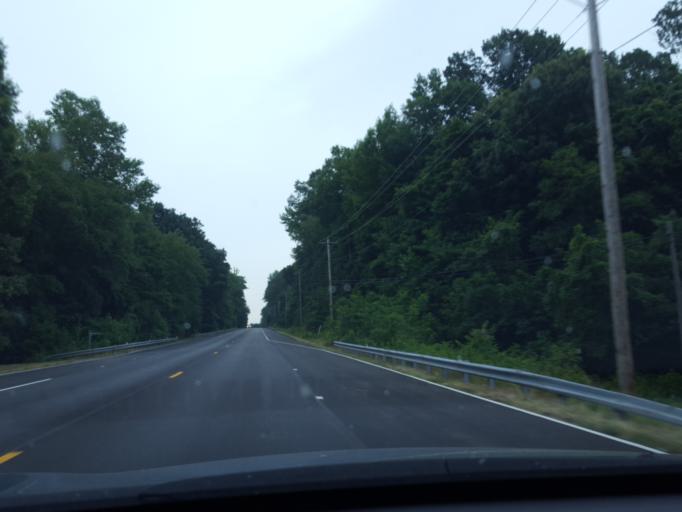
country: US
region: Maryland
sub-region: Saint Mary's County
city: Charlotte Hall
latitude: 38.4138
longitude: -76.8980
